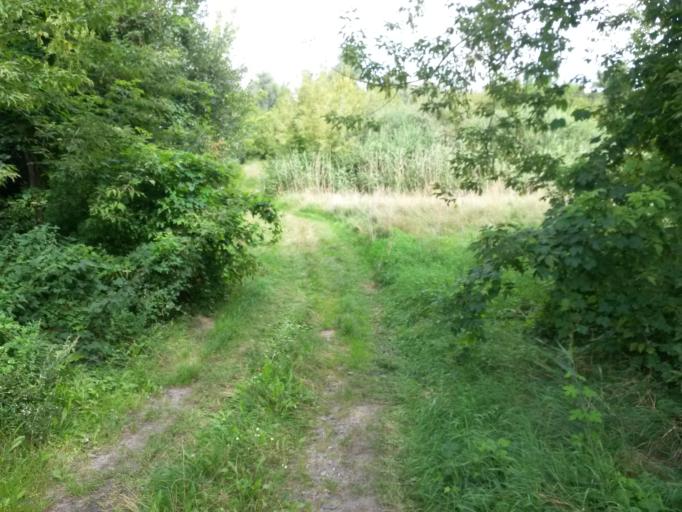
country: DE
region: Brandenburg
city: Oderberg
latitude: 52.8632
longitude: 14.0620
